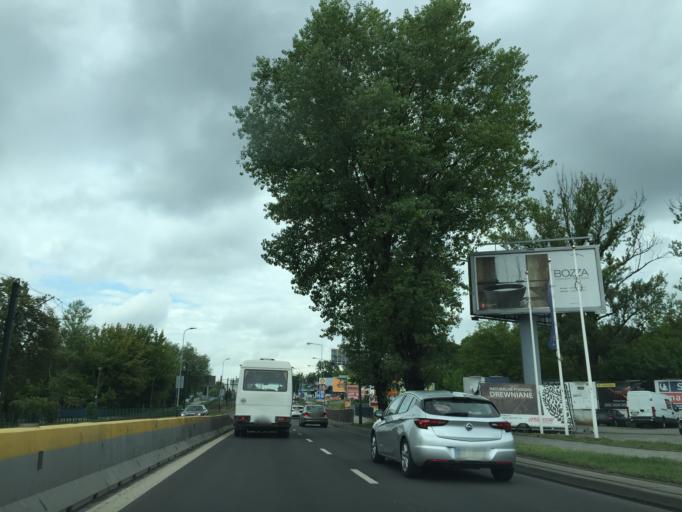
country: PL
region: Lesser Poland Voivodeship
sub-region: Krakow
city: Krakow
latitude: 50.0200
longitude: 19.9318
